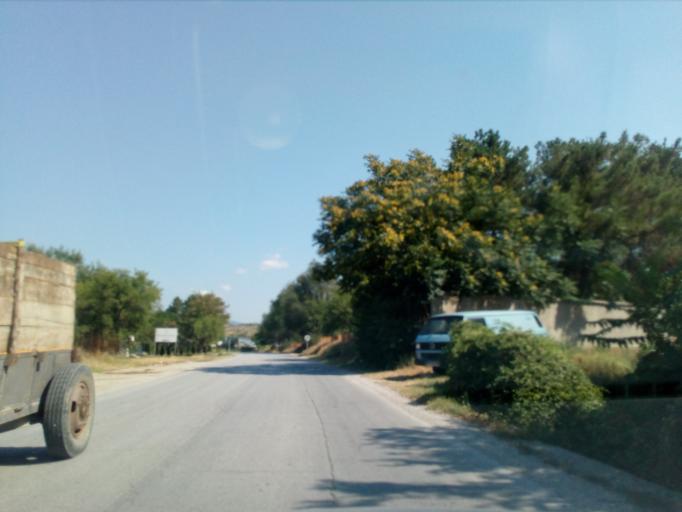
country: MK
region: Veles
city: Veles
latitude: 41.7339
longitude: 21.7777
